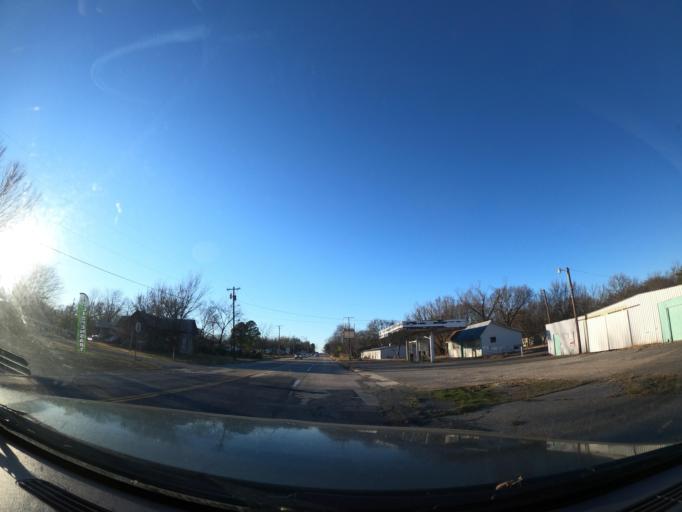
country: US
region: Oklahoma
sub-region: Pittsburg County
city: Hartshorne
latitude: 34.8418
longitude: -95.5452
